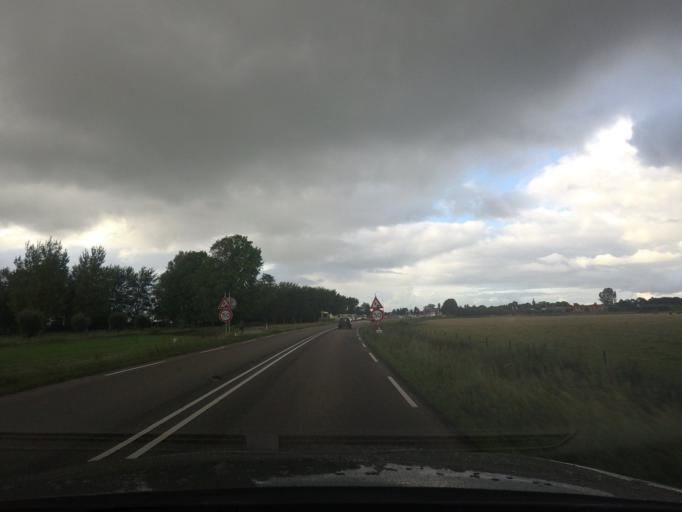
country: NL
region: North Holland
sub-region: Gemeente Castricum
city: Castricum
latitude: 52.5578
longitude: 4.6893
